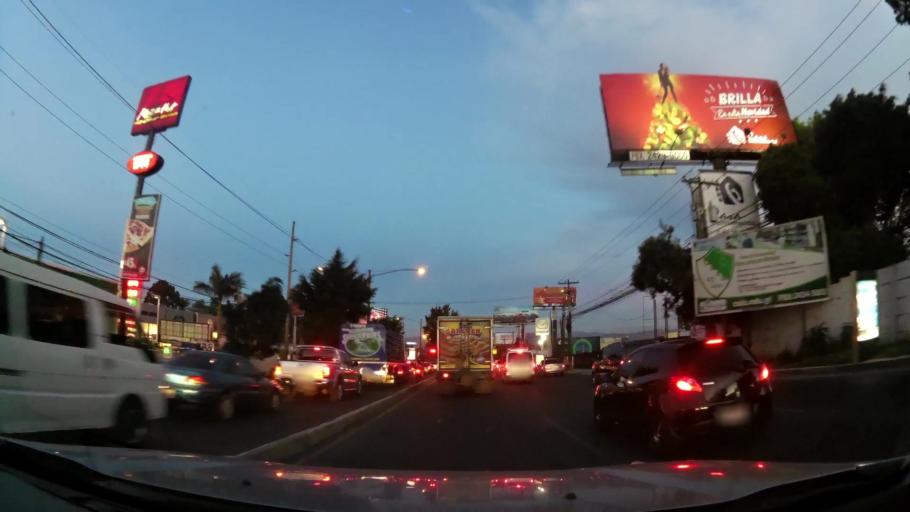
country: GT
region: Guatemala
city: Mixco
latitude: 14.6344
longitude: -90.5852
